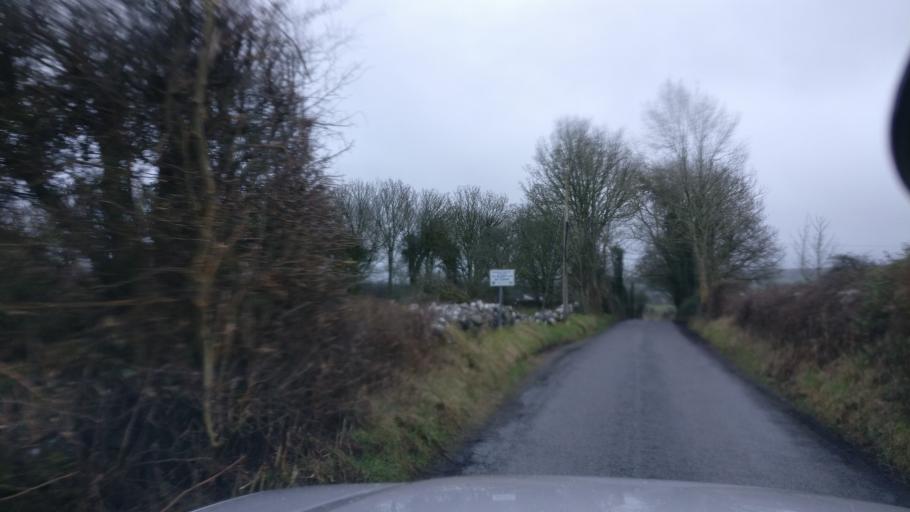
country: IE
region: Connaught
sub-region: County Galway
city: Loughrea
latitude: 53.1868
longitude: -8.6597
